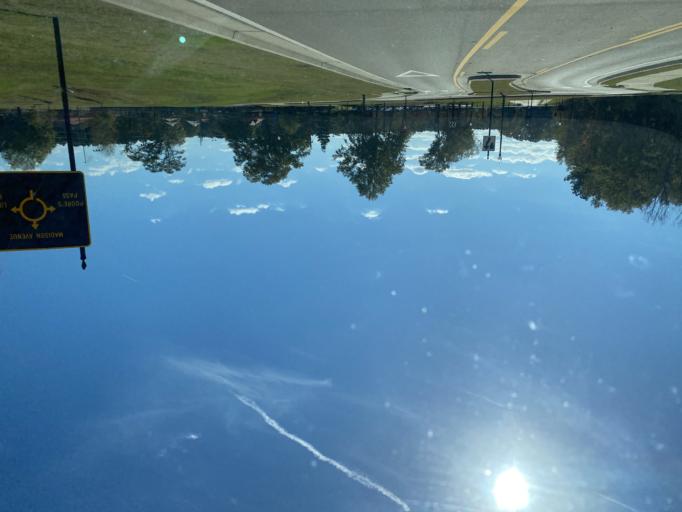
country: US
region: Mississippi
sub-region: Madison County
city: Madison
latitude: 32.4625
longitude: -90.1275
